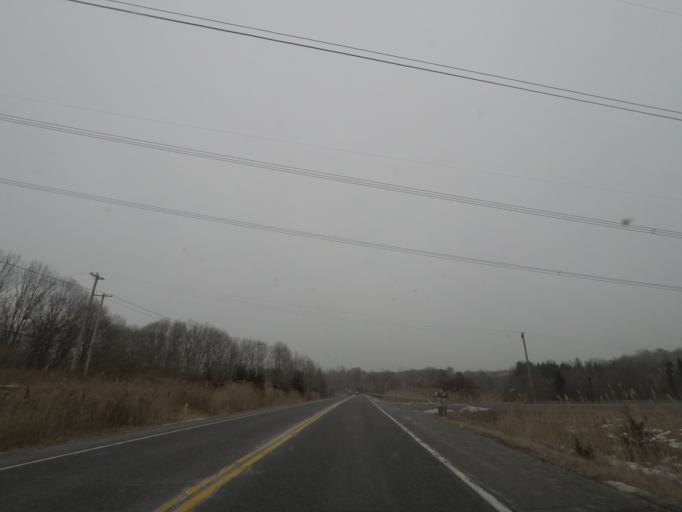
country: US
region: New York
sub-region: Albany County
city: Delmar
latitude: 42.5597
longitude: -73.8132
